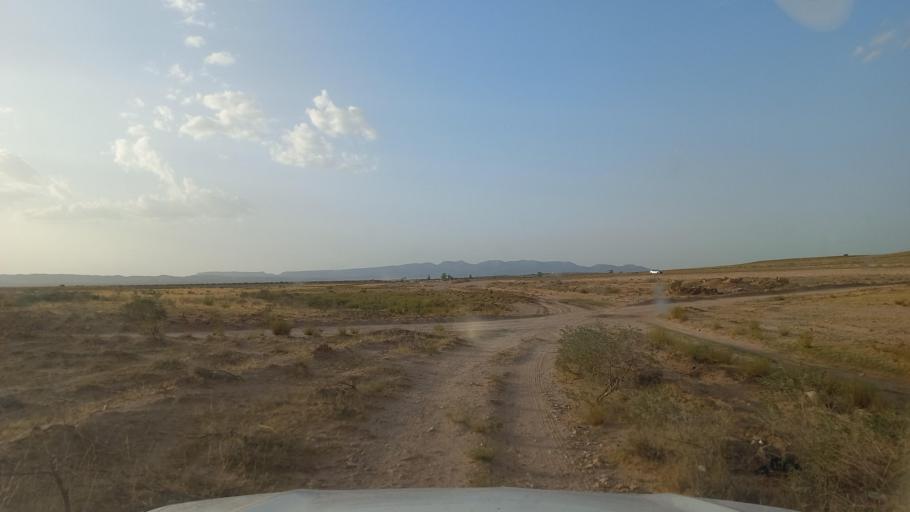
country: TN
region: Al Qasrayn
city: Sbiba
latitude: 35.3080
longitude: 9.0736
